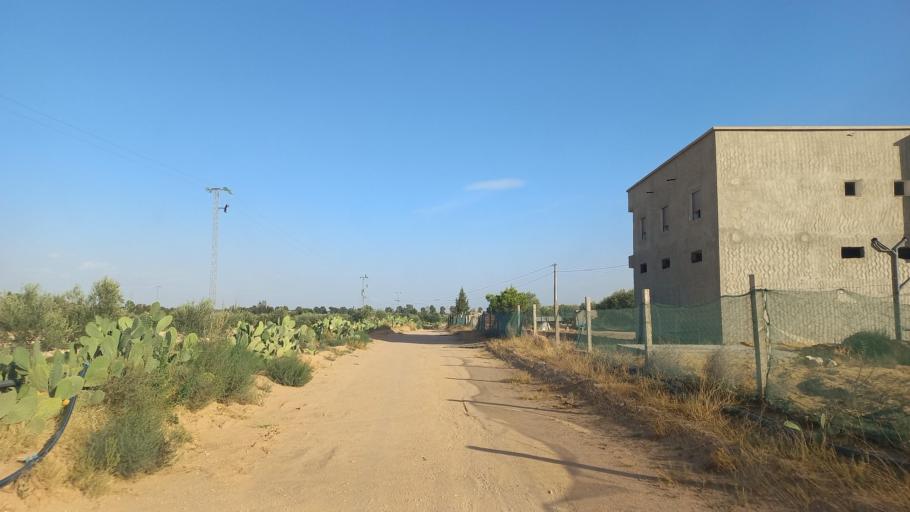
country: TN
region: Al Qasrayn
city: Kasserine
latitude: 35.2650
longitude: 9.0233
